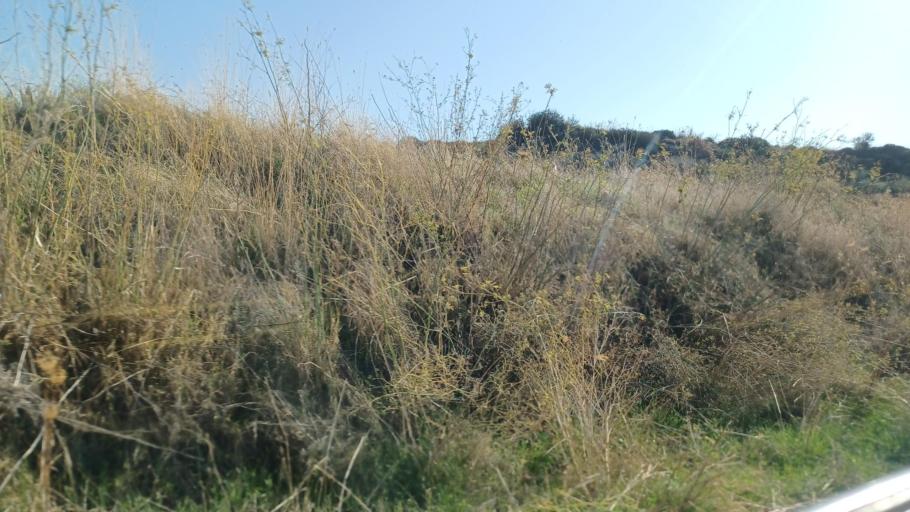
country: CY
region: Pafos
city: Polis
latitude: 35.0120
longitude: 32.4458
